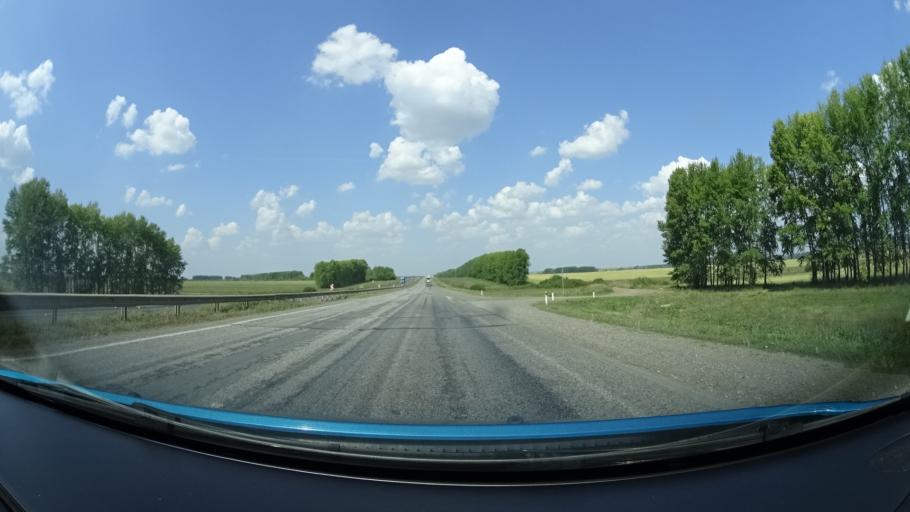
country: RU
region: Bashkortostan
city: Dmitriyevka
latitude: 54.7151
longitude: 55.2004
